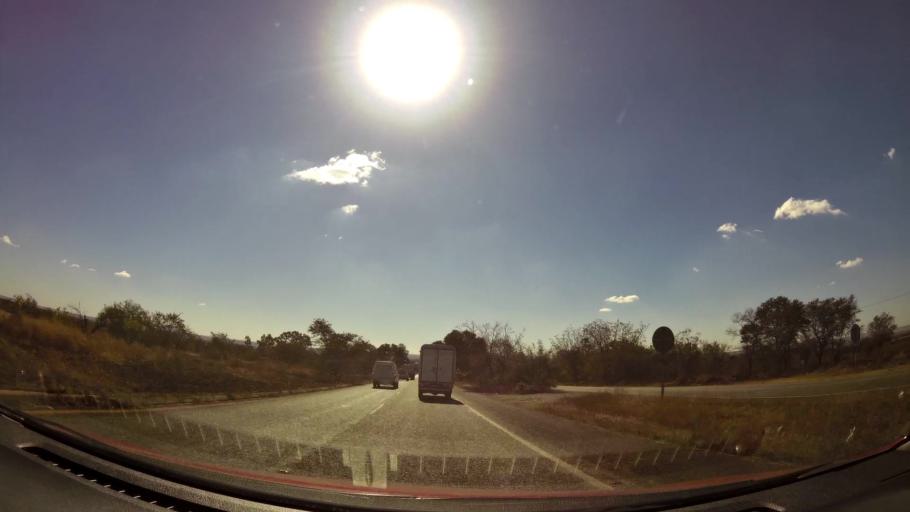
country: ZA
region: Gauteng
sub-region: West Rand District Municipality
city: Carletonville
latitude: -26.3768
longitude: 27.4074
